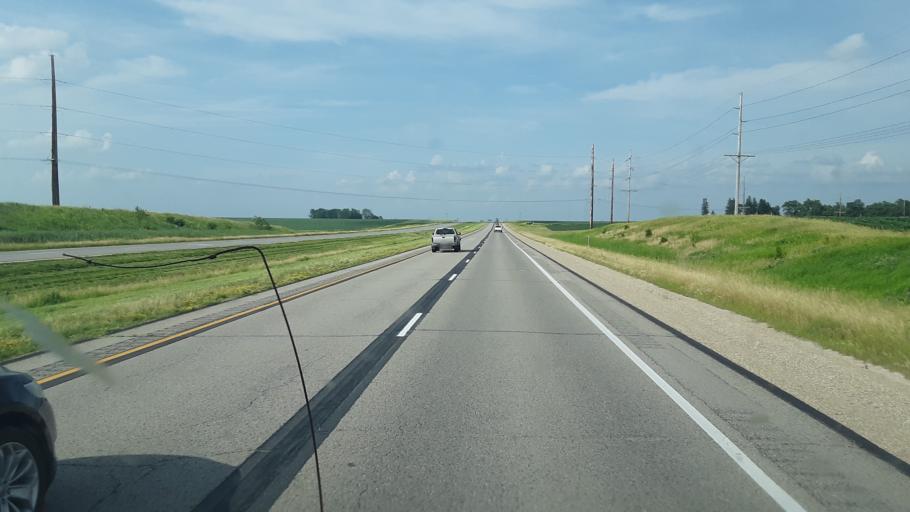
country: US
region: Iowa
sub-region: Jasper County
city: Baxter
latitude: 41.9049
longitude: -93.1724
